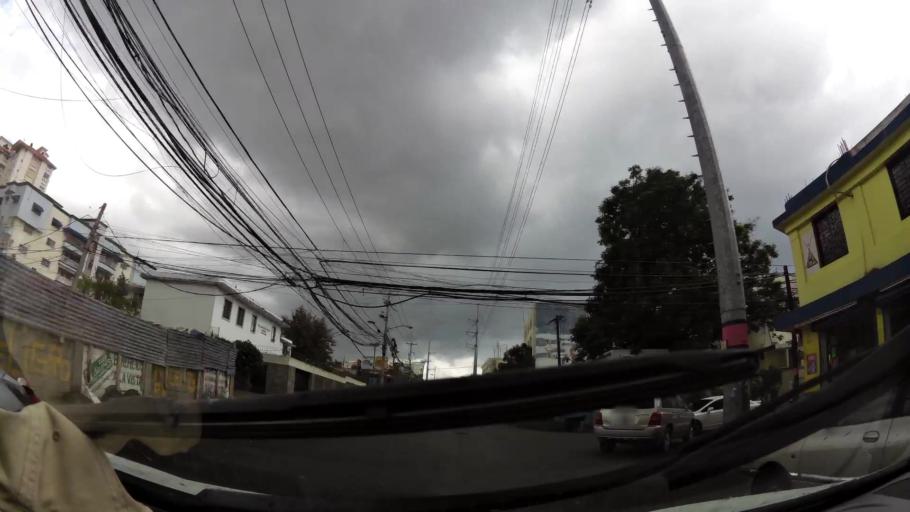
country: DO
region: Nacional
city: Ciudad Nueva
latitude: 18.4660
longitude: -69.9118
